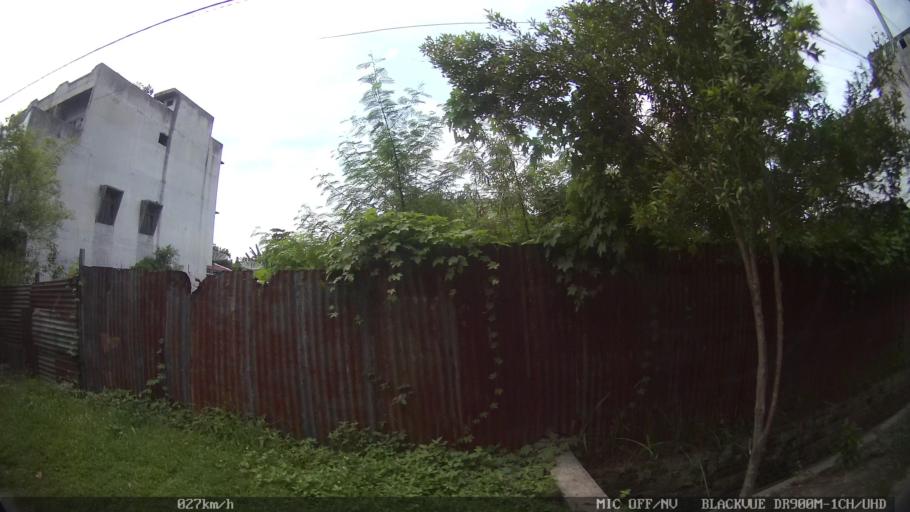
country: ID
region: North Sumatra
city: Percut
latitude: 3.5614
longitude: 98.8677
